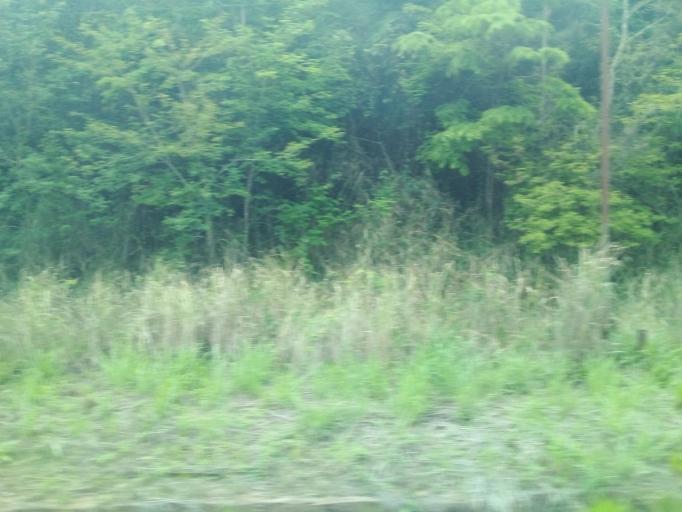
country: BR
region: Minas Gerais
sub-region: Nova Era
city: Nova Era
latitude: -19.7284
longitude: -42.9840
